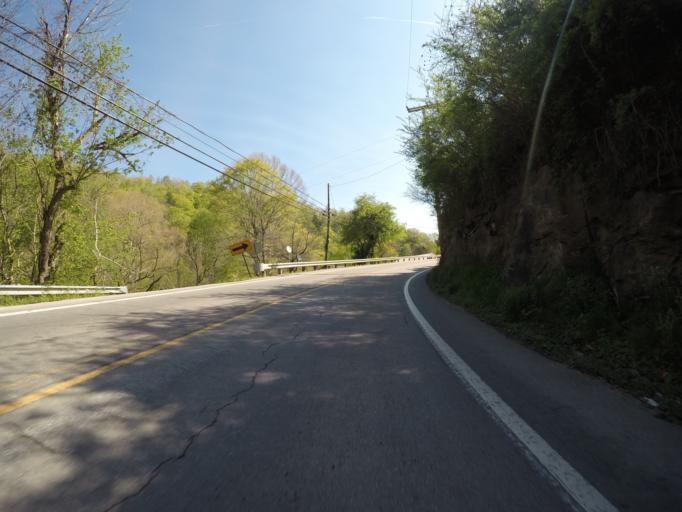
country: US
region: West Virginia
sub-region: Kanawha County
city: Clendenin
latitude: 38.4986
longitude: -81.3482
